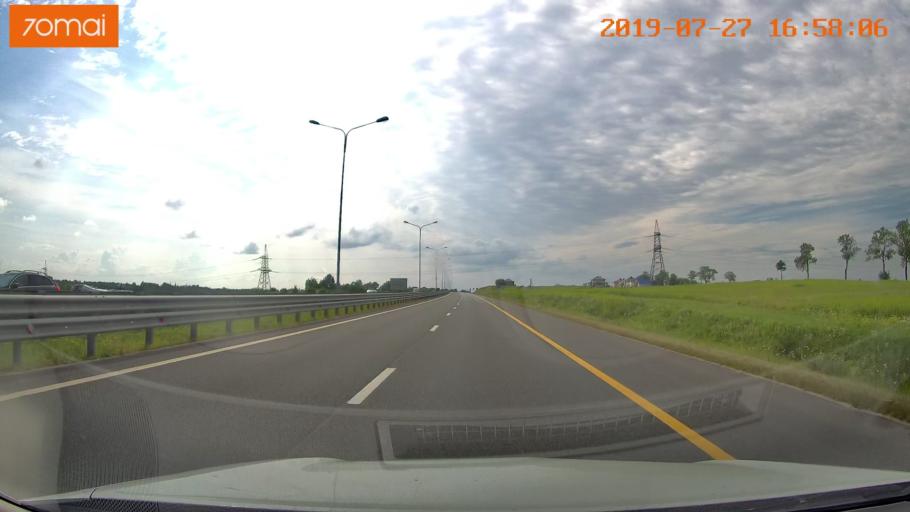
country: RU
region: Kaliningrad
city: Bol'shoe Isakovo
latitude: 54.7012
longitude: 20.6917
